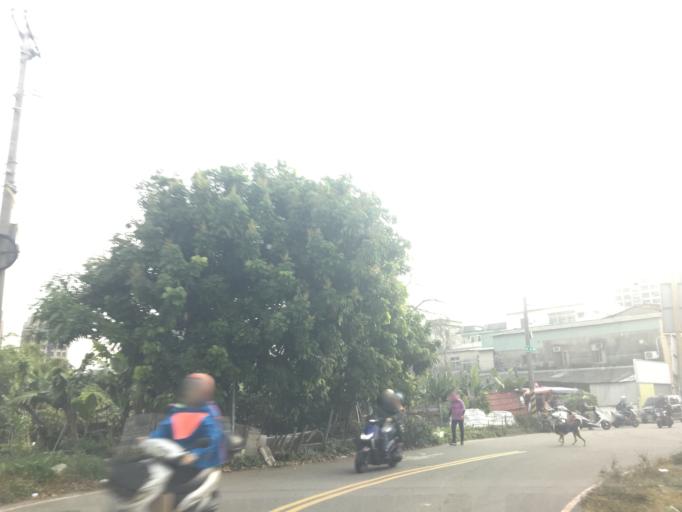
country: TW
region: Taiwan
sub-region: Taichung City
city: Taichung
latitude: 24.1921
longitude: 120.6993
